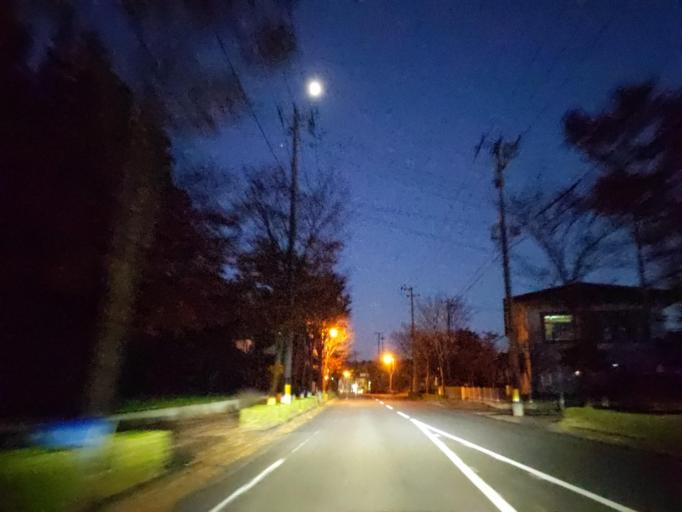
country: JP
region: Fukushima
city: Sukagawa
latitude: 37.2998
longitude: 140.3736
